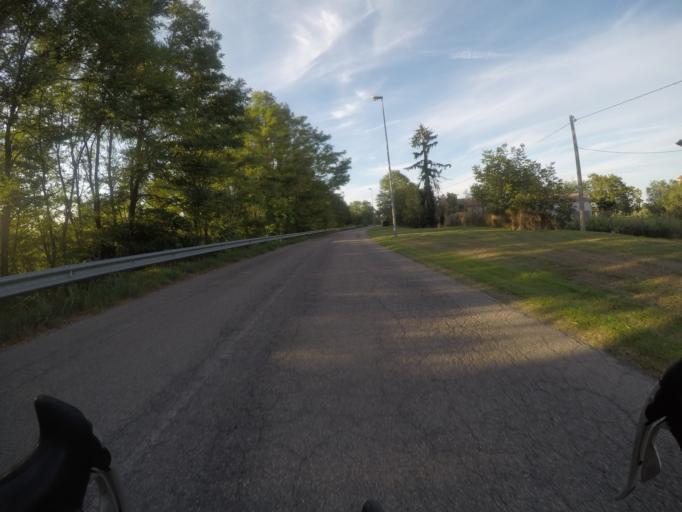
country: IT
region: Veneto
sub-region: Provincia di Rovigo
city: Castelguglielmo
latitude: 45.0066
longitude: 11.5632
